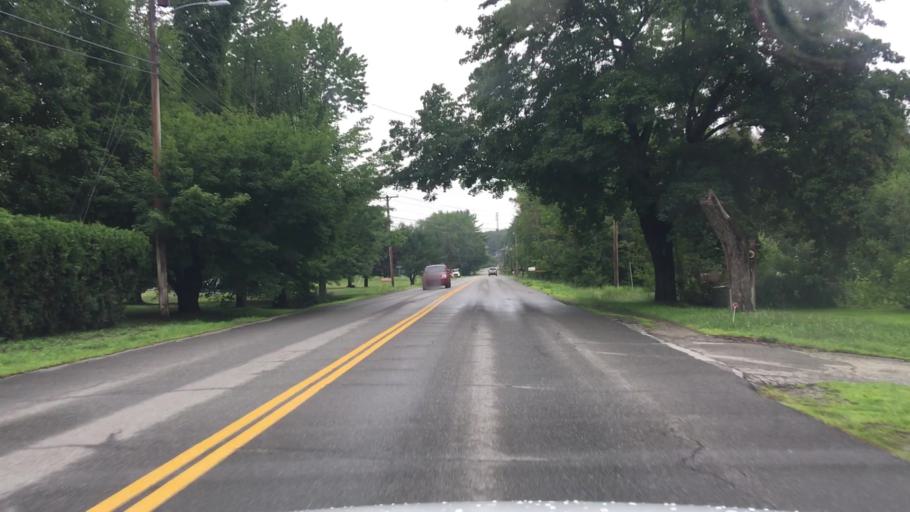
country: US
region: Maine
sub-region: Kennebec County
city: Augusta
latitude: 44.3507
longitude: -69.8023
